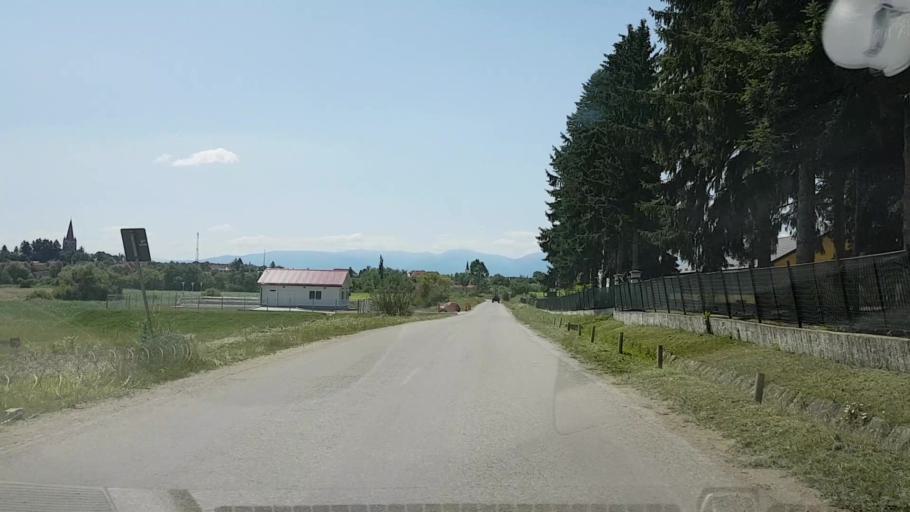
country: RO
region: Brasov
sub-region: Comuna Cincu
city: Cincu
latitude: 45.9237
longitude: 24.7977
